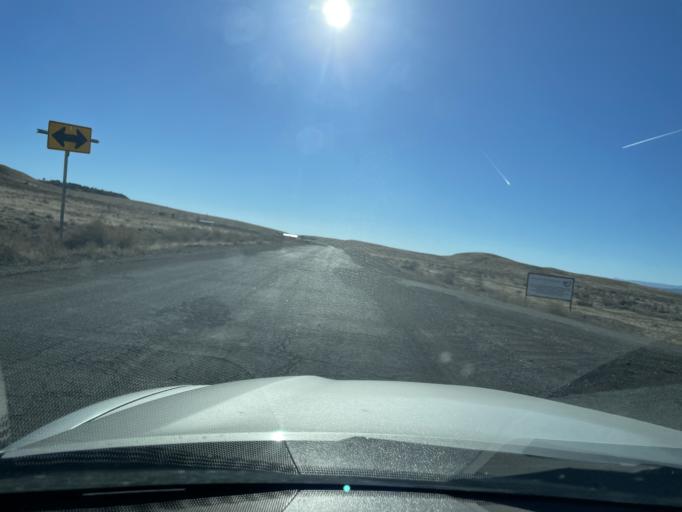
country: US
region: Colorado
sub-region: Mesa County
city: Loma
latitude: 39.2039
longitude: -109.1145
